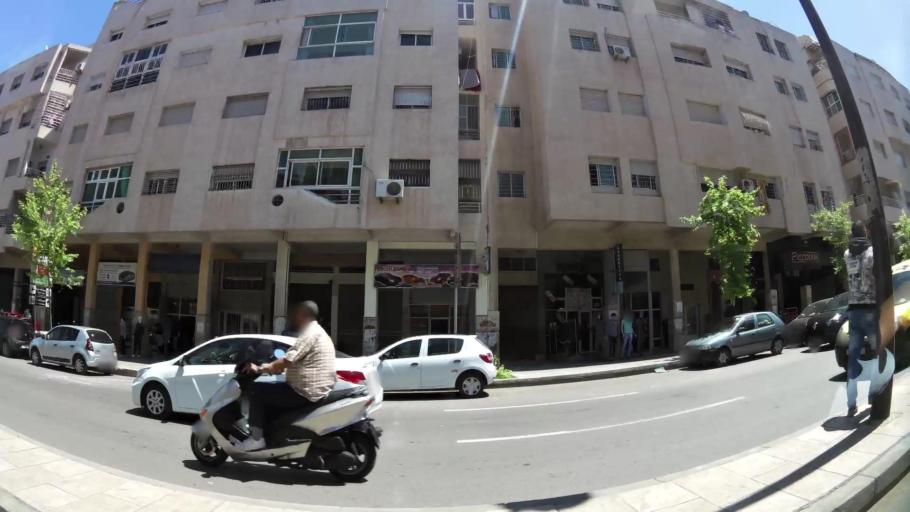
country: MA
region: Fes-Boulemane
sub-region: Fes
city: Fes
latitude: 34.0188
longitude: -4.9872
